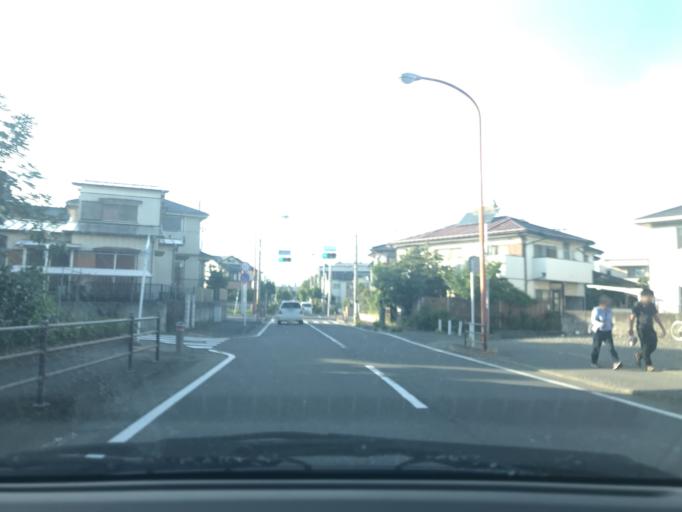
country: JP
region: Kanagawa
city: Fujisawa
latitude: 35.3436
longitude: 139.4624
